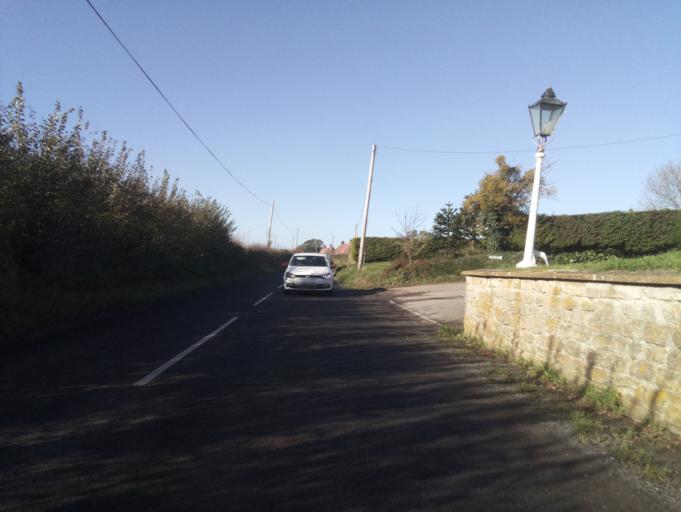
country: GB
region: England
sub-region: Somerset
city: Ilchester
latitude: 50.9706
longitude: -2.7051
